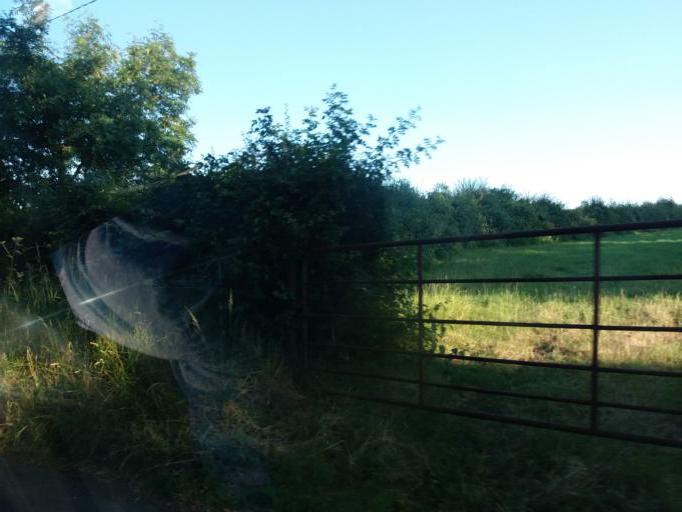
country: IE
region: Leinster
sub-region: An Mhi
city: Ashbourne
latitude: 53.5761
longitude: -6.3675
